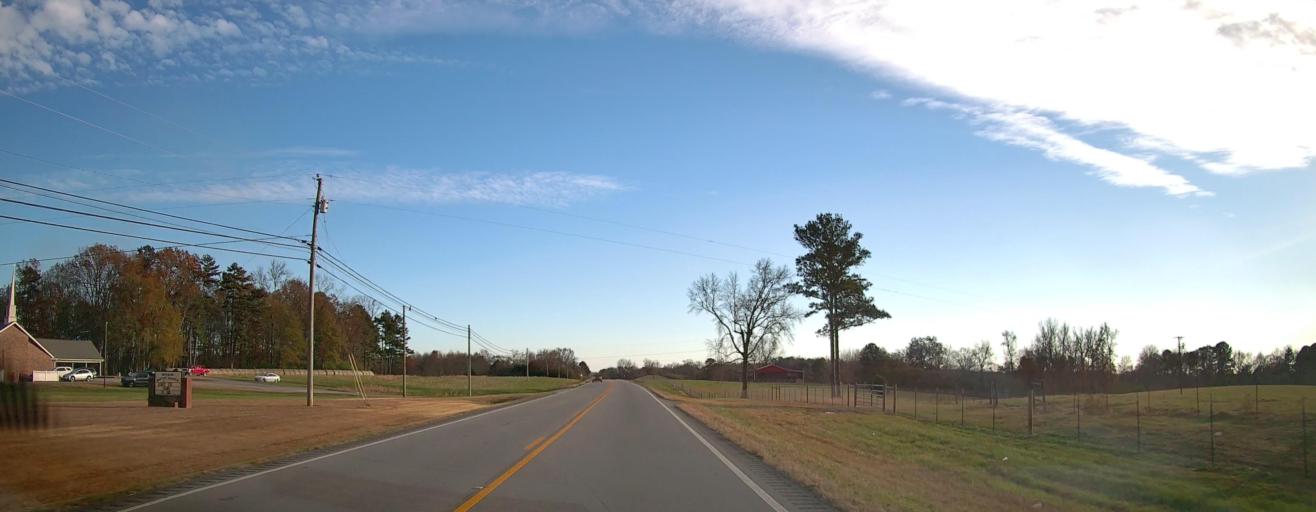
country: US
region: Alabama
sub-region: Marshall County
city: Arab
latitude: 34.3373
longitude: -86.6086
